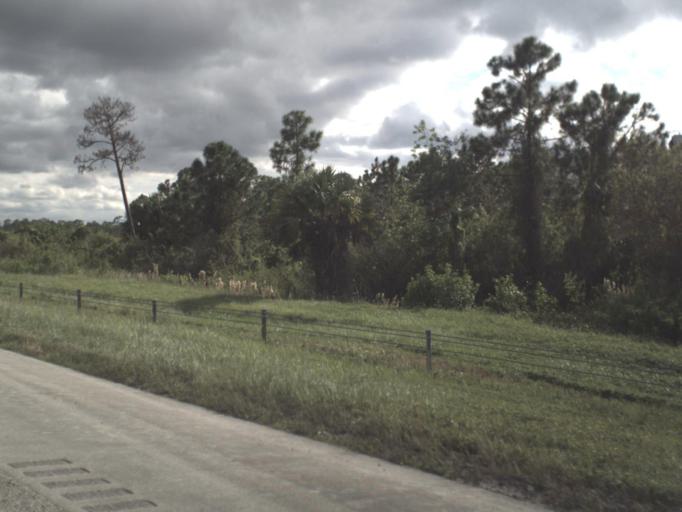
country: US
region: Florida
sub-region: Martin County
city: Palm City
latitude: 27.0960
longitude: -80.2579
